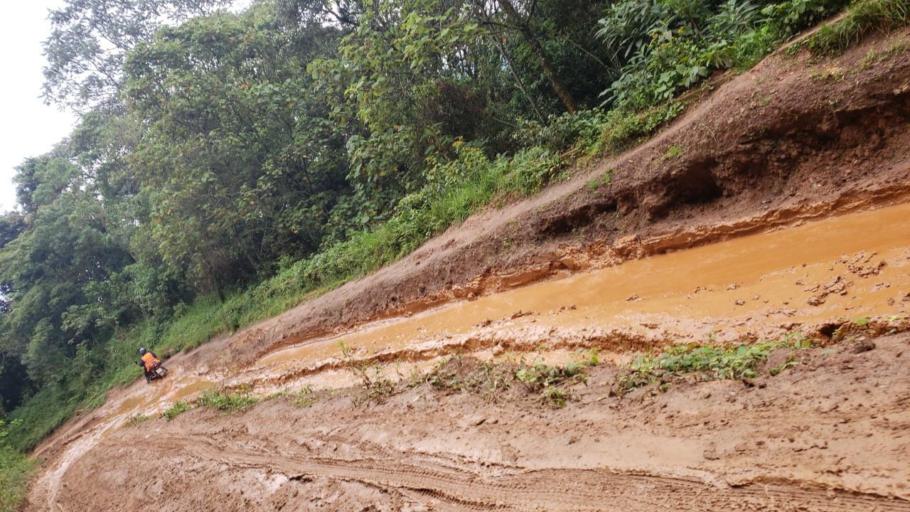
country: CD
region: South Kivu
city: Kabare
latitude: -2.2559
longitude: 28.6473
